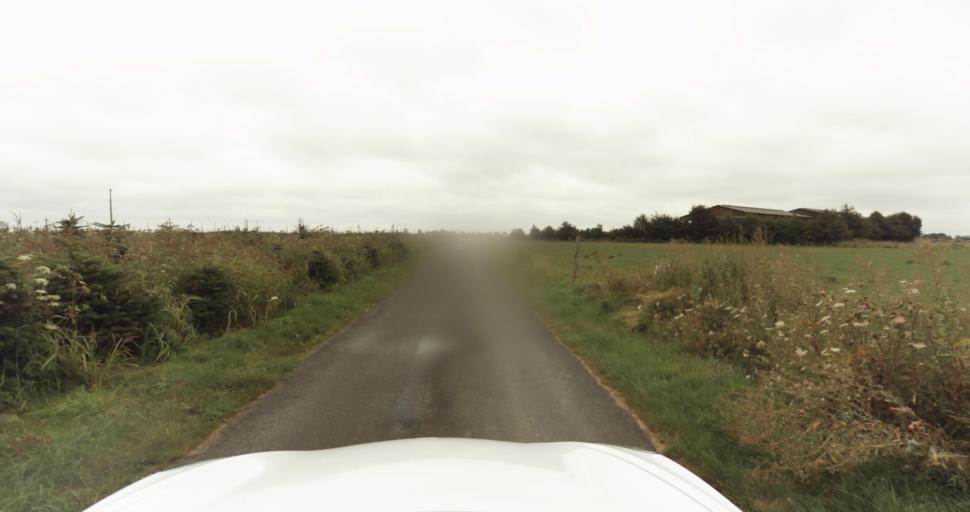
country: FR
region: Haute-Normandie
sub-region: Departement de l'Eure
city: Aviron
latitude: 49.0789
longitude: 1.0717
